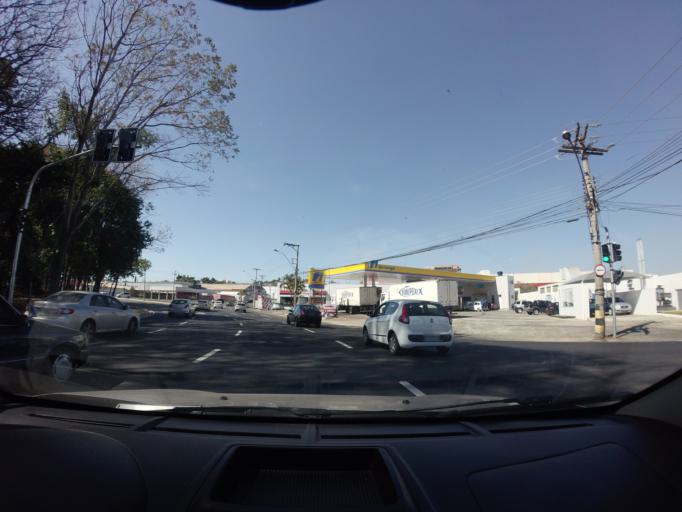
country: BR
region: Sao Paulo
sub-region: Piracicaba
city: Piracicaba
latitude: -22.7260
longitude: -47.6267
